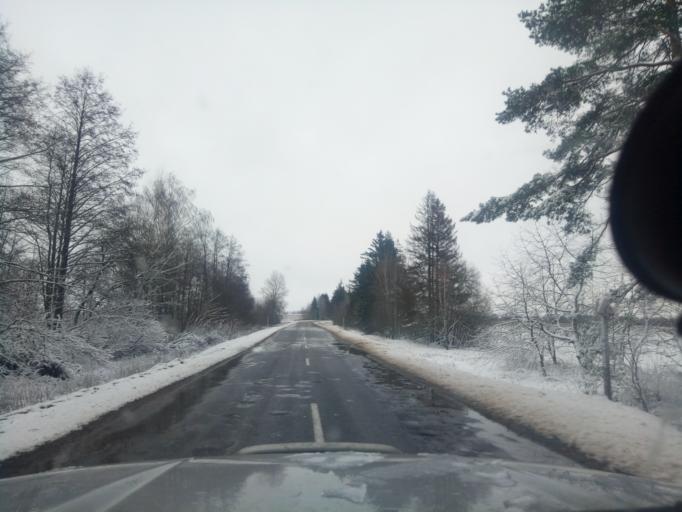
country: BY
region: Minsk
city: Tsimkavichy
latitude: 53.0536
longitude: 26.8962
